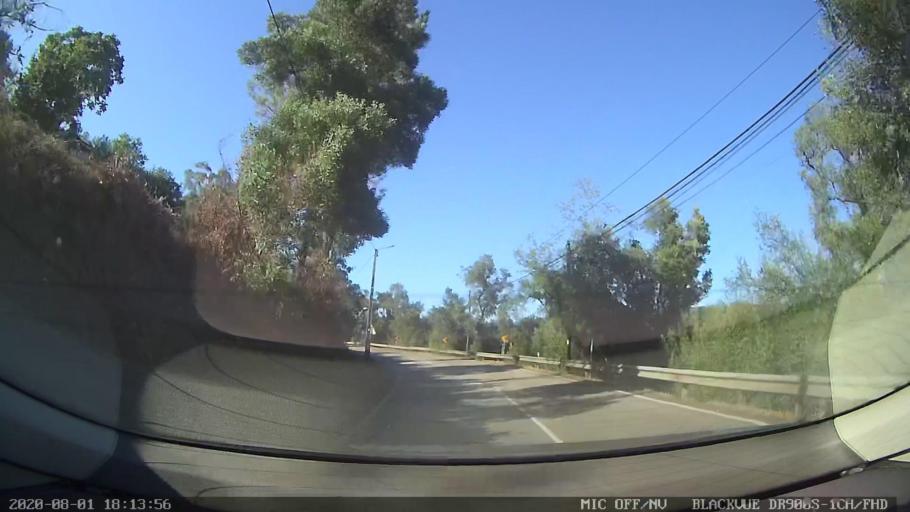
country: PT
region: Porto
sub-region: Pacos de Ferreira
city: Seroa
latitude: 41.2744
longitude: -8.4687
